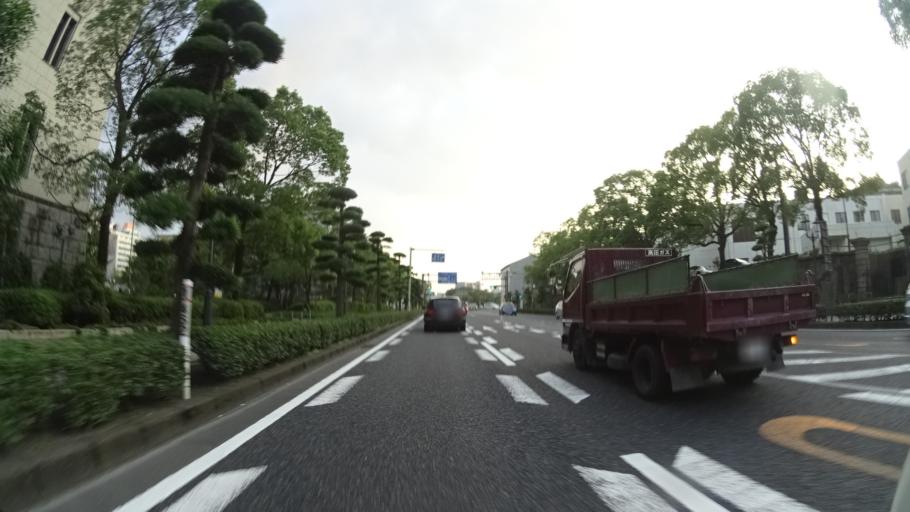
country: JP
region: Kagoshima
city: Kagoshima-shi
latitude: 31.5997
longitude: 130.5571
